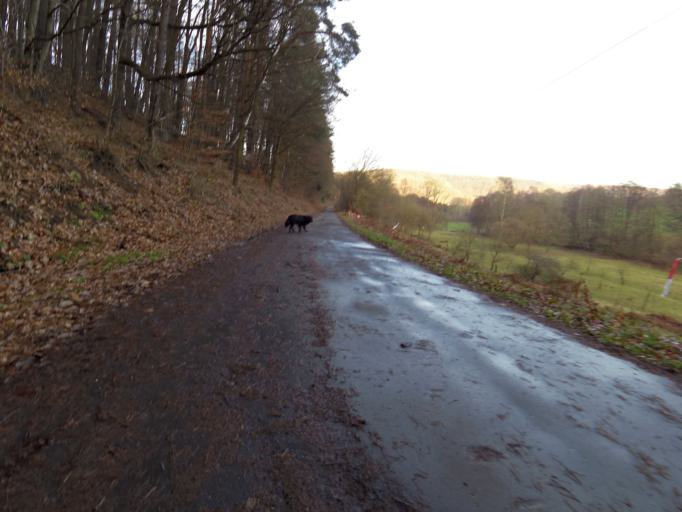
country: DE
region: Lower Saxony
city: Hannoversch Munden
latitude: 51.4675
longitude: 9.6105
